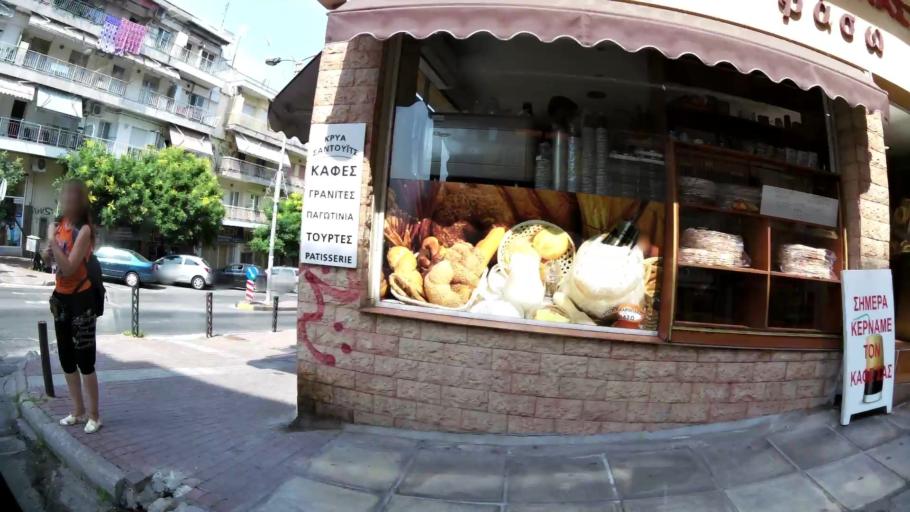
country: GR
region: Central Macedonia
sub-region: Nomos Thessalonikis
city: Agios Pavlos
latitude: 40.6398
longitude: 22.9517
